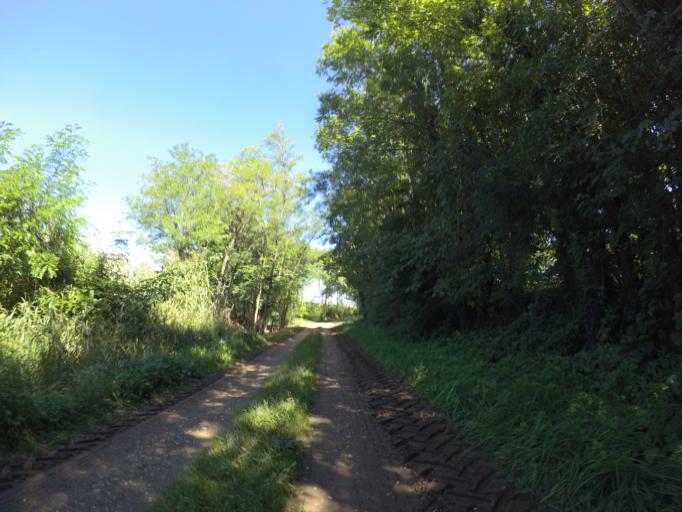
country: IT
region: Friuli Venezia Giulia
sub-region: Provincia di Udine
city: Bertiolo
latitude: 45.9522
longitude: 13.0892
